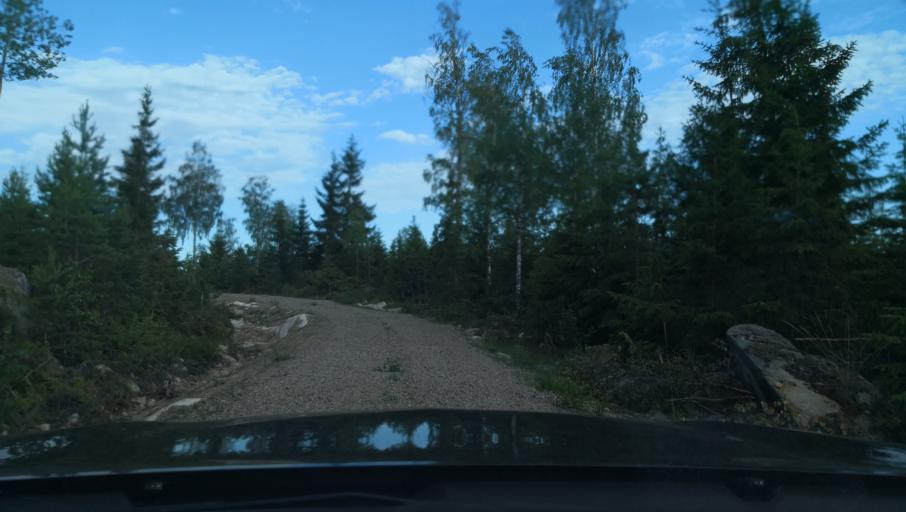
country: SE
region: Dalarna
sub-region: Smedjebackens Kommun
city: Smedjebacken
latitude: 60.0694
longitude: 15.3025
